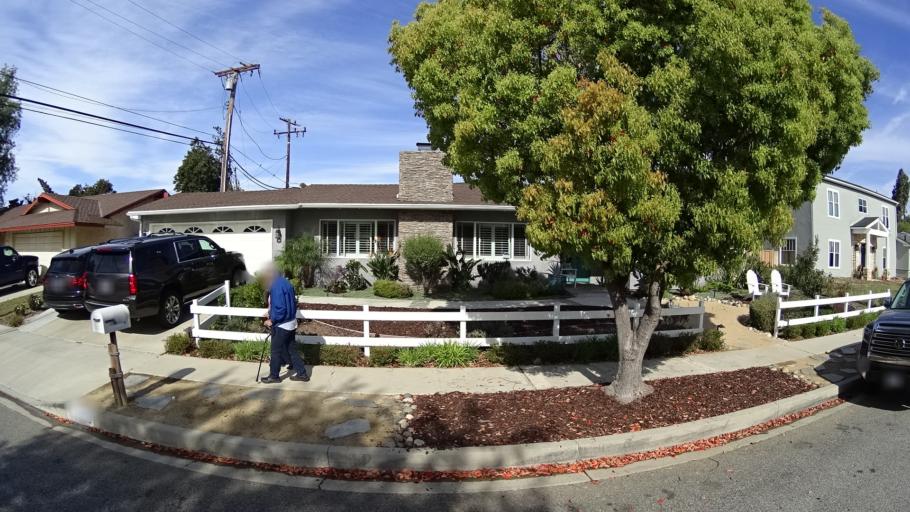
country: US
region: California
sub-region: Ventura County
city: Thousand Oaks
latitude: 34.1970
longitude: -118.8806
